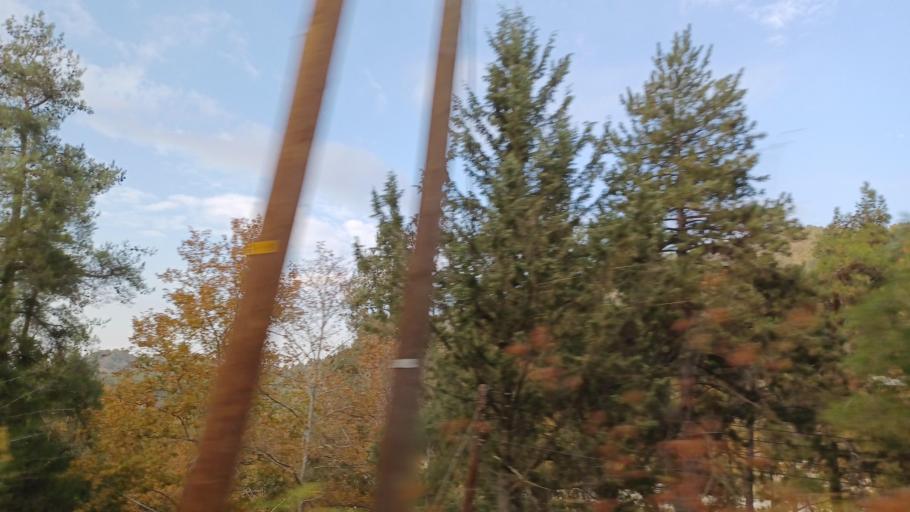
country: CY
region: Lefkosia
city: Kakopetria
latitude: 34.9681
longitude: 32.9193
